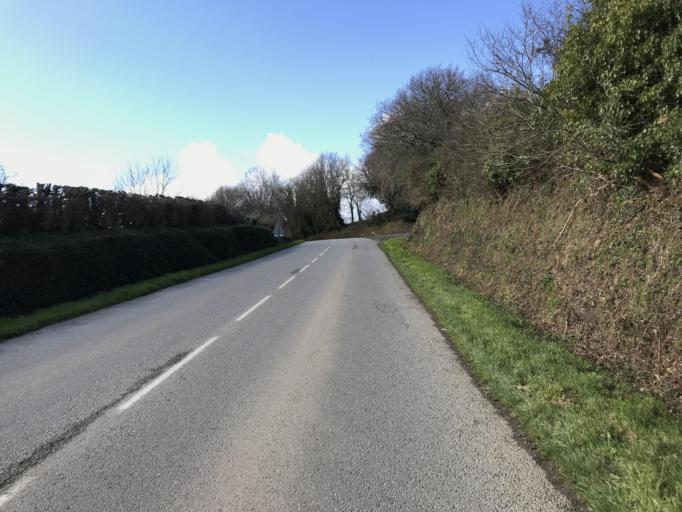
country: FR
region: Brittany
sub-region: Departement du Finistere
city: Loperhet
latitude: 48.3810
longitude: -4.3306
